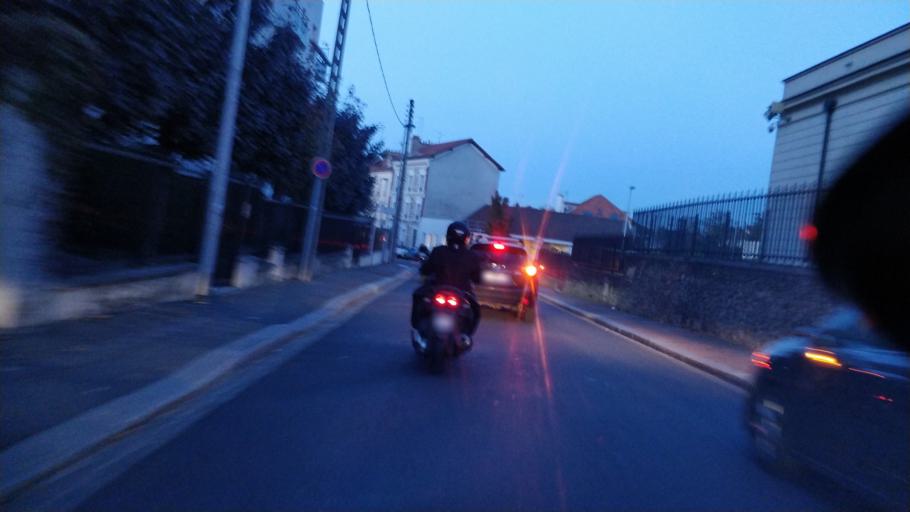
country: FR
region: Ile-de-France
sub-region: Departement de Seine-Saint-Denis
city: Villemomble
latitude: 48.8845
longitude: 2.5105
